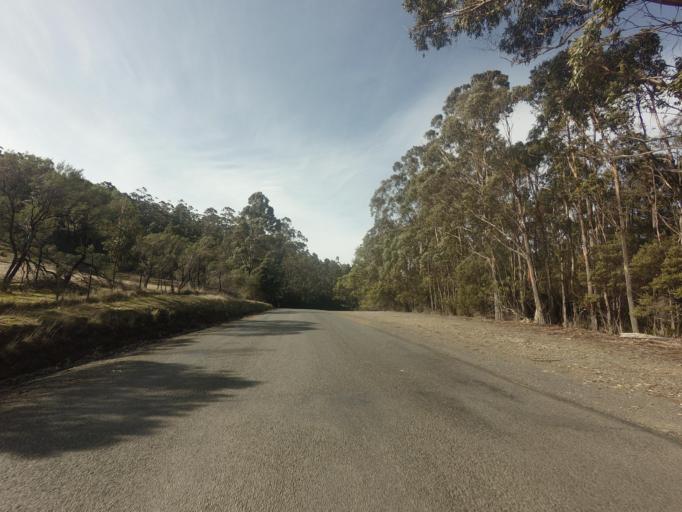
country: AU
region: Tasmania
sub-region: Kingborough
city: Kettering
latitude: -43.1702
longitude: 147.1985
